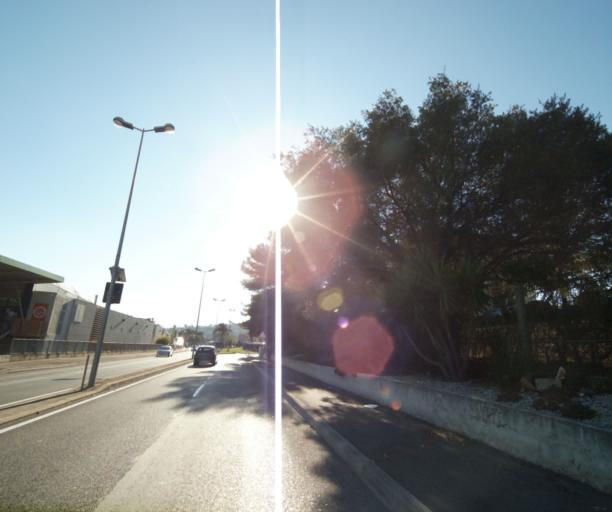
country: FR
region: Provence-Alpes-Cote d'Azur
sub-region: Departement des Bouches-du-Rhone
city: La Ciotat
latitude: 43.1881
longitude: 5.6013
